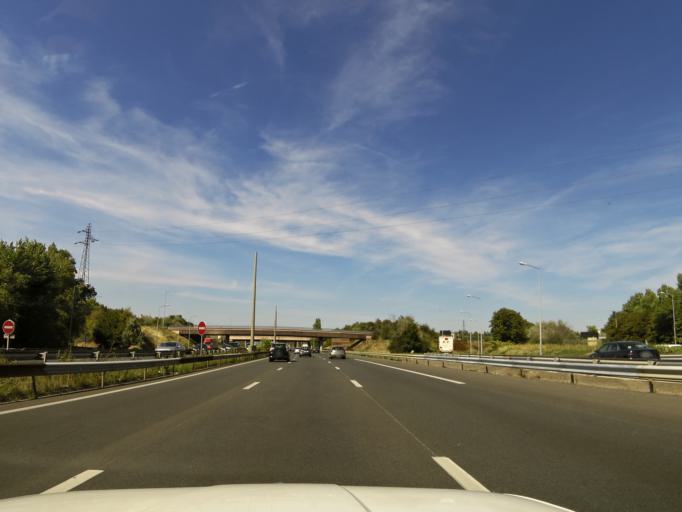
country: FR
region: Rhone-Alpes
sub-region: Departement du Rhone
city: Feyzin
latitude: 45.6761
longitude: 4.8481
